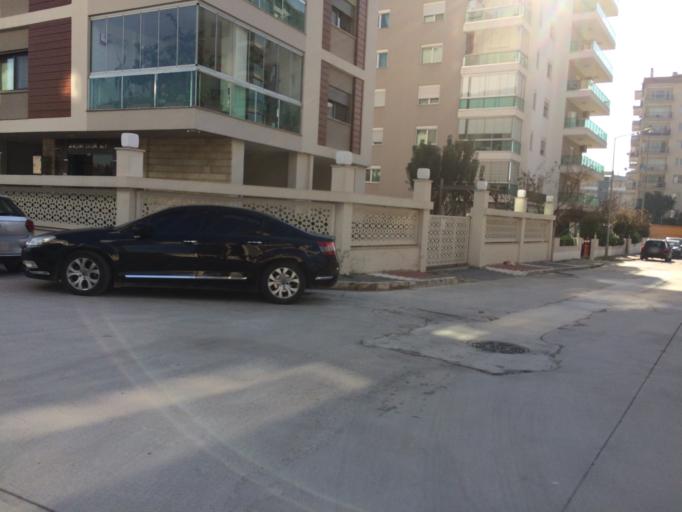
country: TR
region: Izmir
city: Karsiyaka
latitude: 38.4878
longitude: 27.0581
